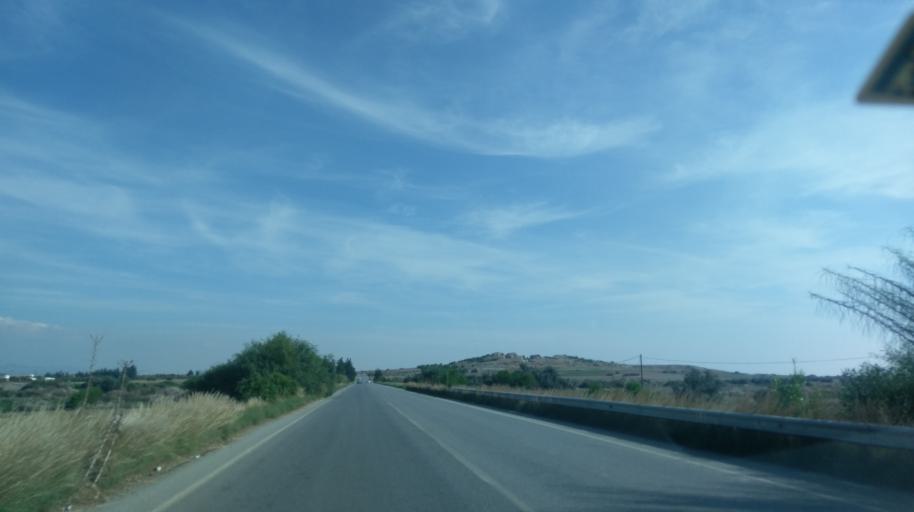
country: CY
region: Ammochostos
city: Lefkonoiko
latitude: 35.2503
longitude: 33.6195
